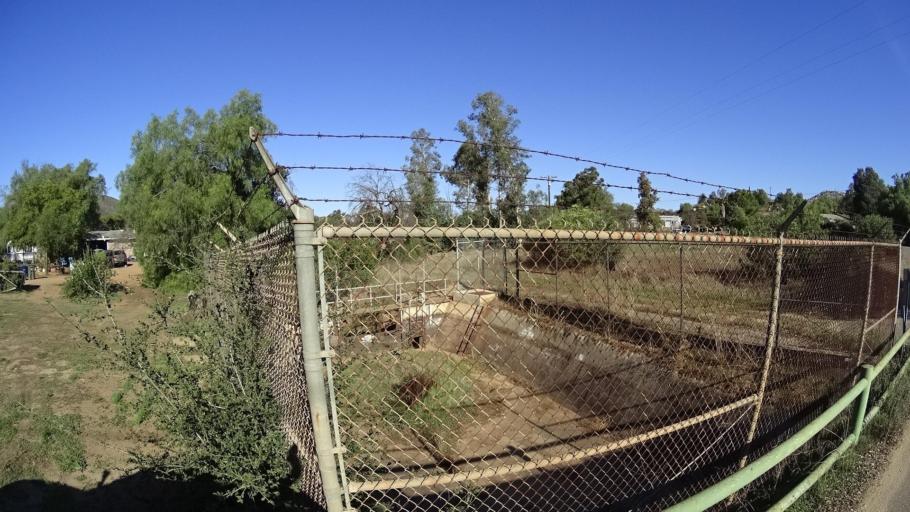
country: MX
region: Baja California
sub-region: Tijuana
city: Villa del Campo
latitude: 32.6200
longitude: -116.7647
